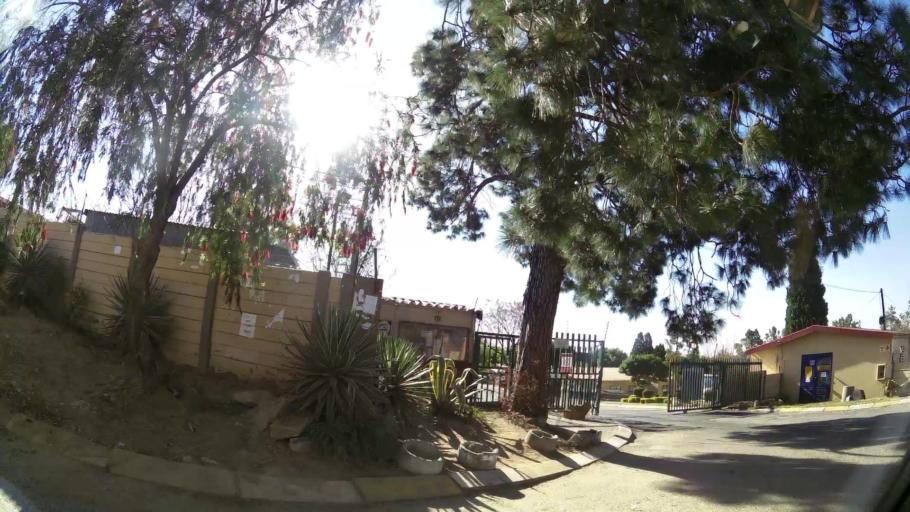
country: ZA
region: Gauteng
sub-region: City of Johannesburg Metropolitan Municipality
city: Diepsloot
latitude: -26.0223
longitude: 27.9706
